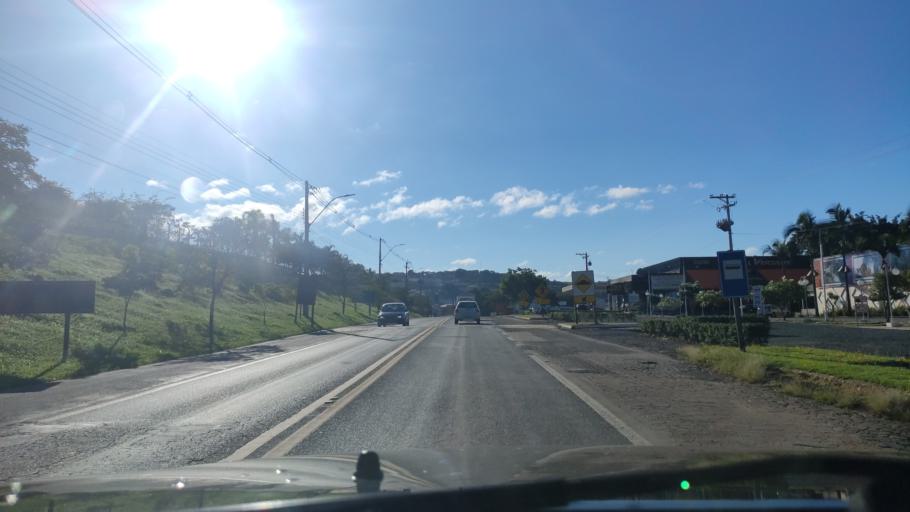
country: BR
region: Sao Paulo
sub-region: Socorro
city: Socorro
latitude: -22.5767
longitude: -46.5281
